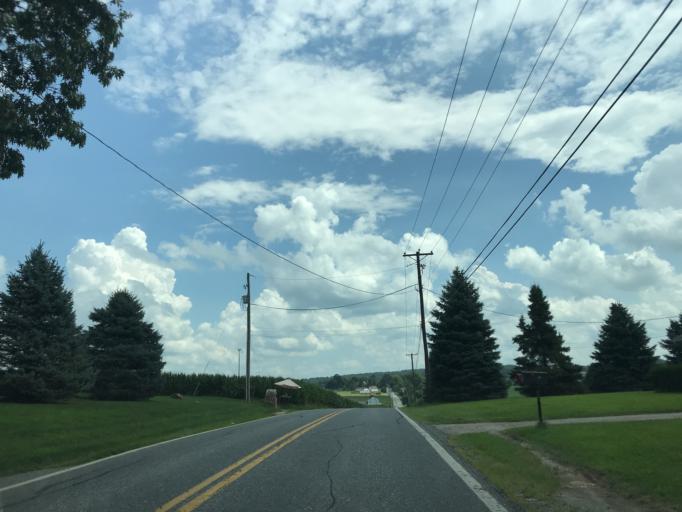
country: US
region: Pennsylvania
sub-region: York County
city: Dallastown
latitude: 39.8399
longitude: -76.6276
